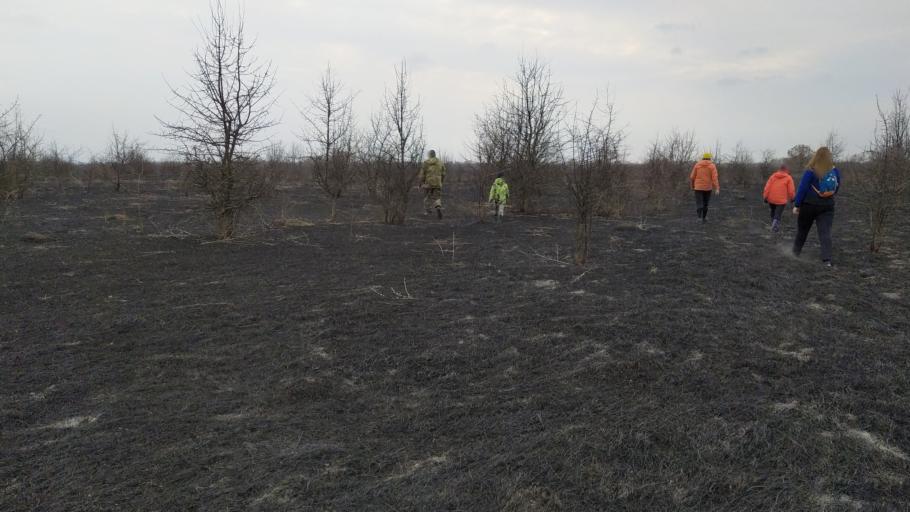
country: RU
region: Rostov
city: Semikarakorsk
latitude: 47.5483
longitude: 40.6814
